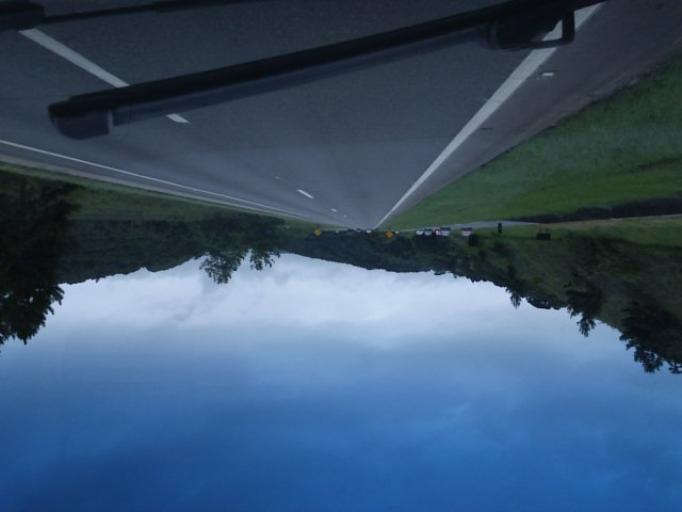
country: BR
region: Parana
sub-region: Campina Grande Do Sul
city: Campina Grande do Sul
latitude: -25.1303
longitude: -48.8573
